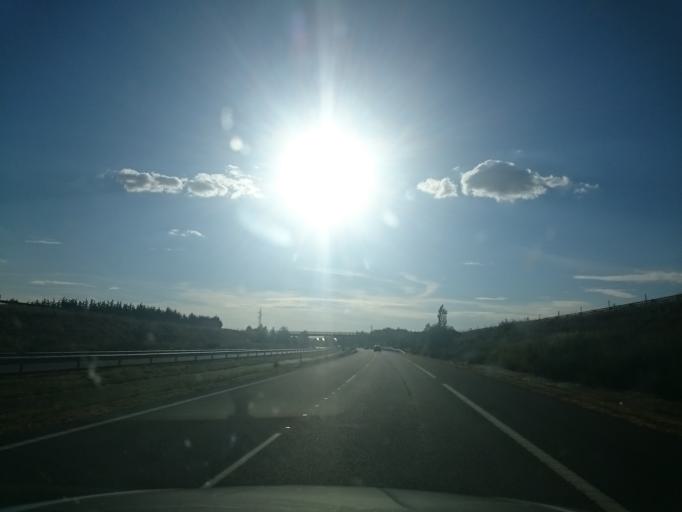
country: ES
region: Castille and Leon
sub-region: Provincia de Burgos
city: Melgar de Fernamental
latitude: 42.4112
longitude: -4.2417
